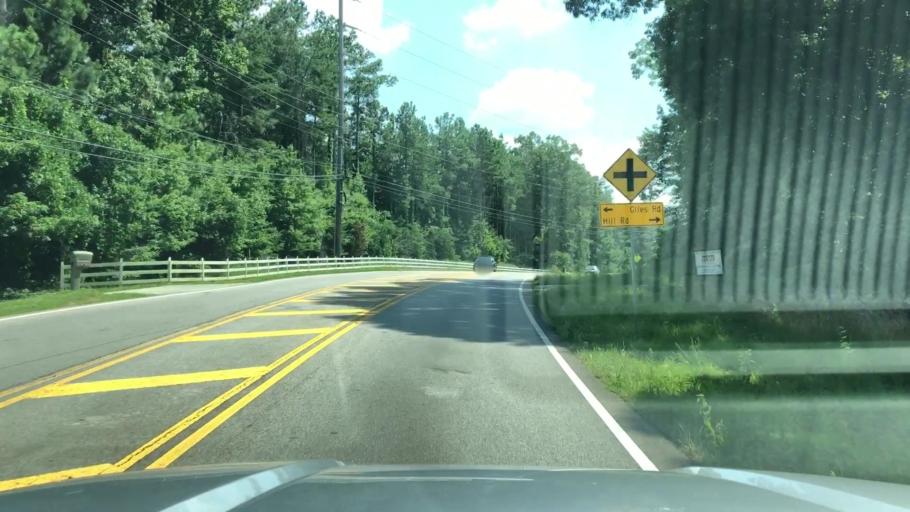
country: US
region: Georgia
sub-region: Cobb County
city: Acworth
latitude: 34.0283
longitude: -84.6952
